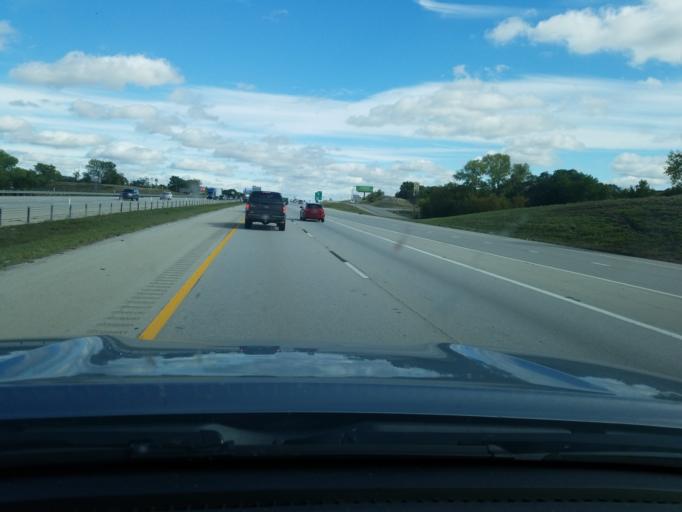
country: US
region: Texas
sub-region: Parker County
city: Hudson Oaks
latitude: 32.7519
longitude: -97.6857
